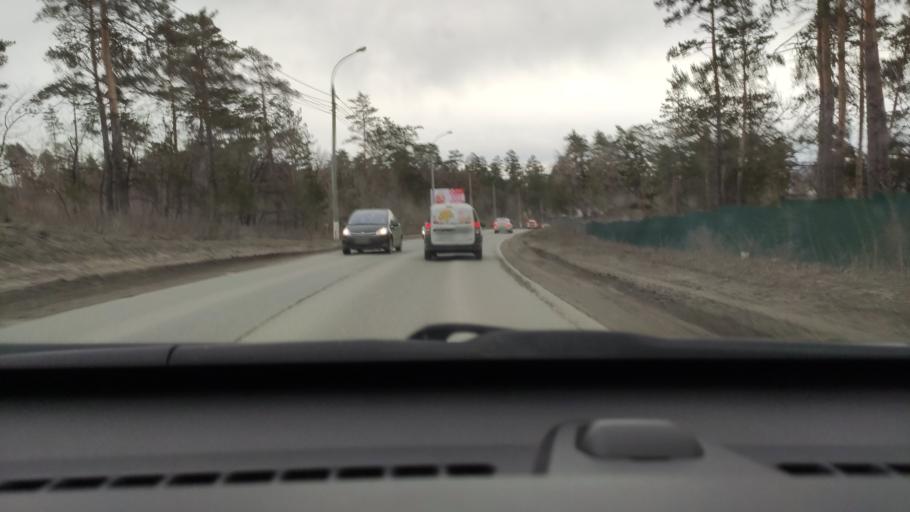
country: RU
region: Samara
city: Tol'yatti
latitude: 53.4794
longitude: 49.3510
